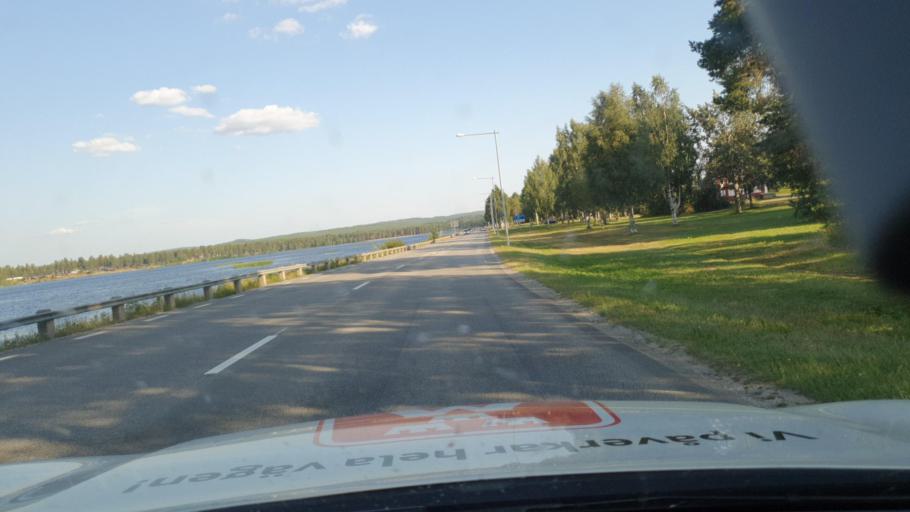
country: SE
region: Vaesterbotten
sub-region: Lycksele Kommun
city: Lycksele
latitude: 64.6030
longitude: 18.6748
